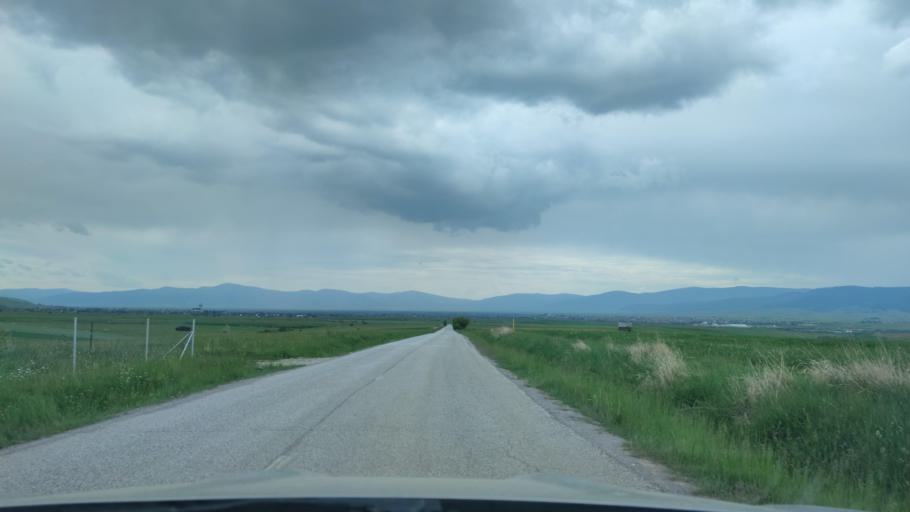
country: RO
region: Harghita
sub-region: Comuna Ditrau
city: Ditrau
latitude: 46.8401
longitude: 25.4970
